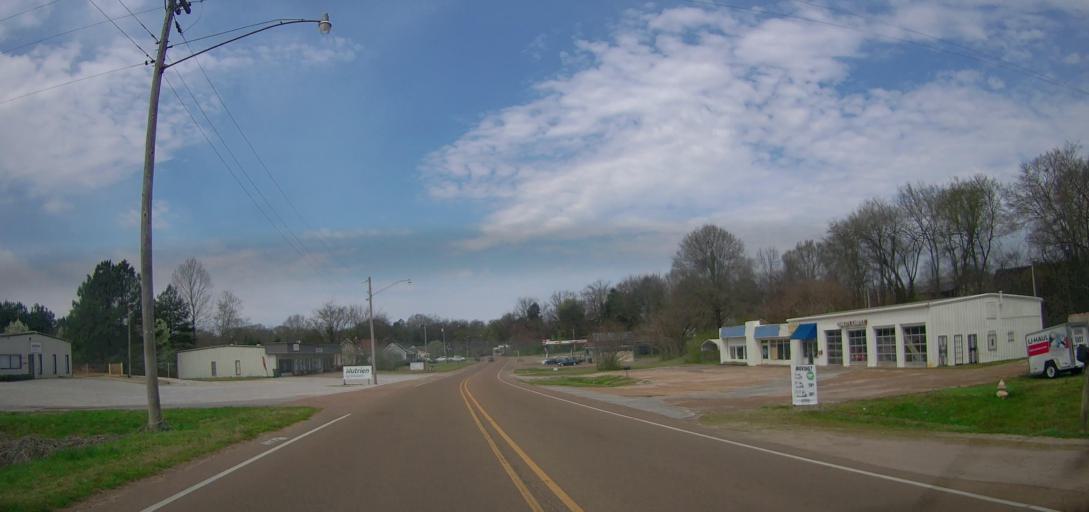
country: US
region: Mississippi
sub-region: Marshall County
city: Holly Springs
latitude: 34.7661
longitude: -89.4346
